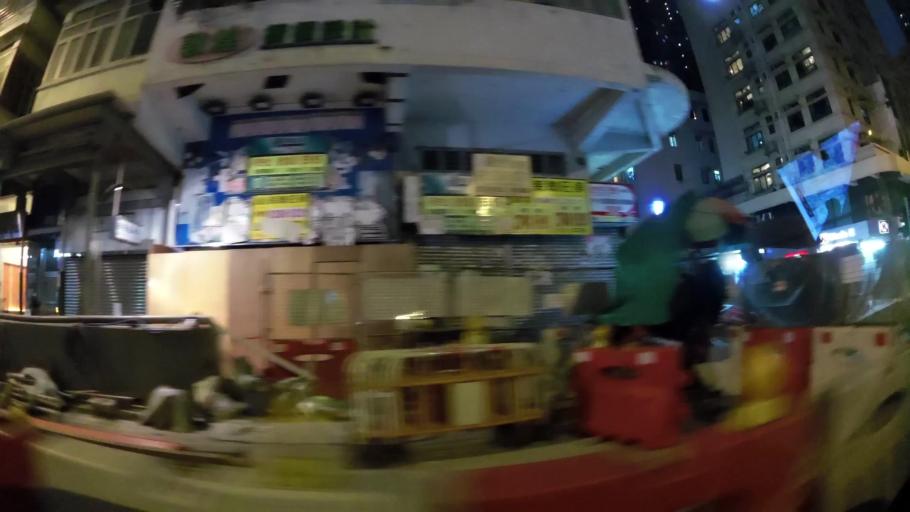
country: HK
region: Kowloon City
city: Kowloon
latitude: 22.3178
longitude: 114.1876
